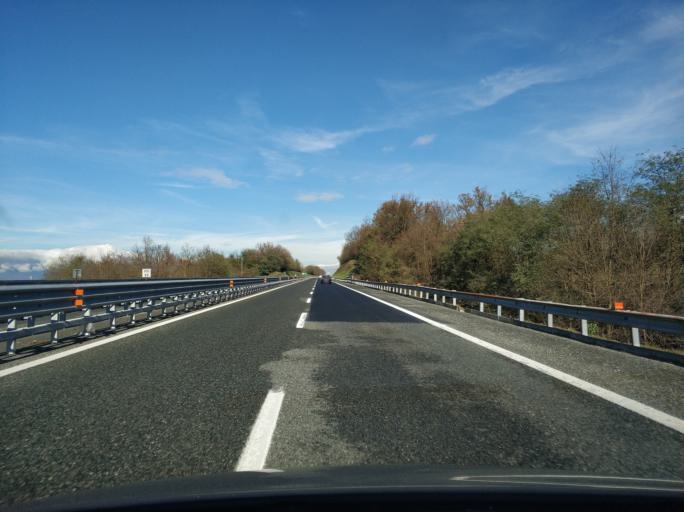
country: IT
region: Piedmont
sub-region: Provincia di Torino
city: San Giusto Canavese
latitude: 45.2991
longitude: 7.8166
